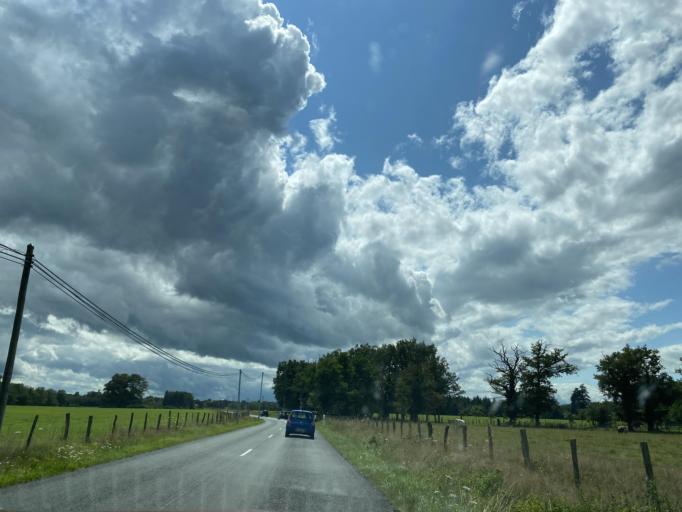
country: FR
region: Auvergne
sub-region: Departement du Puy-de-Dome
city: Peschadoires
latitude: 45.8097
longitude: 3.4821
